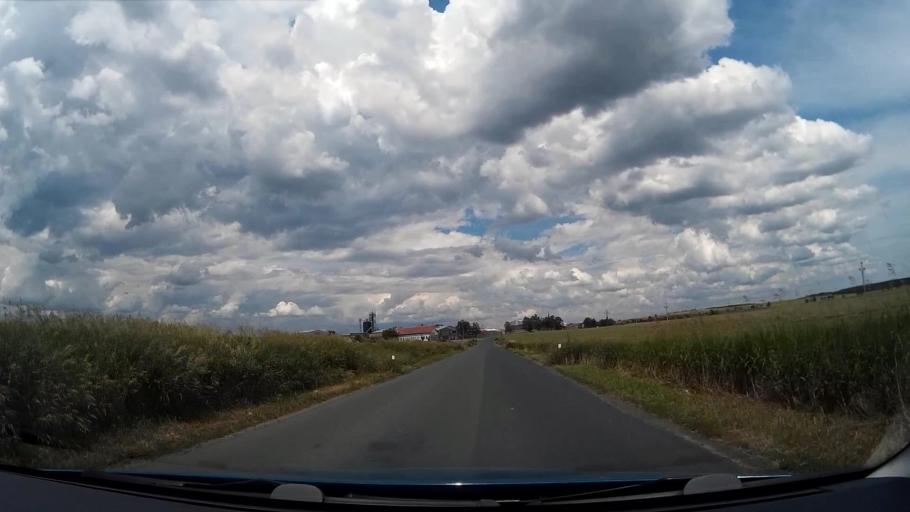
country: CZ
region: South Moravian
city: Orechov
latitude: 49.1015
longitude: 16.5252
